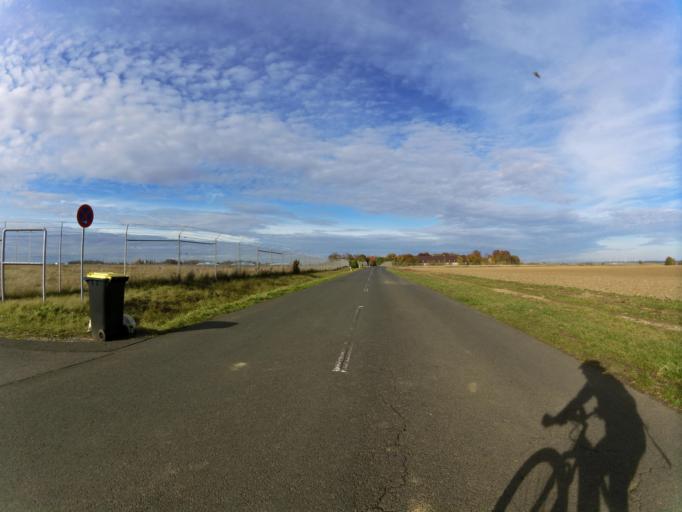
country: DE
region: Bavaria
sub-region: Regierungsbezirk Unterfranken
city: Gaukonigshofen
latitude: 49.6486
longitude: 9.9821
